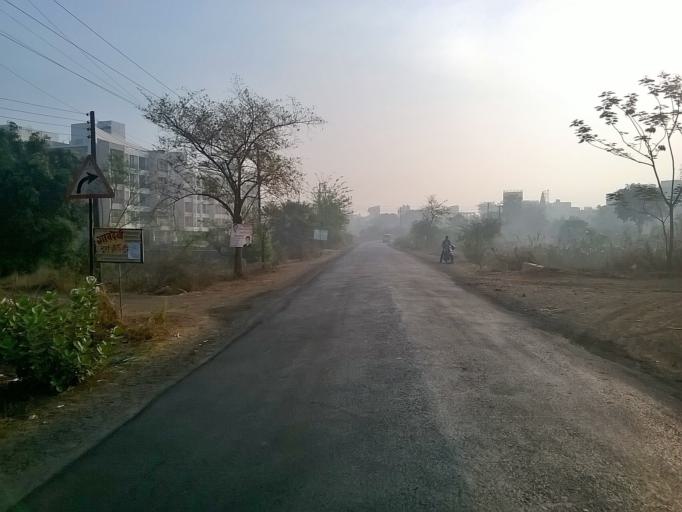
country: IN
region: Maharashtra
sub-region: Raigarh
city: Kalundri
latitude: 19.0103
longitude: 73.1563
